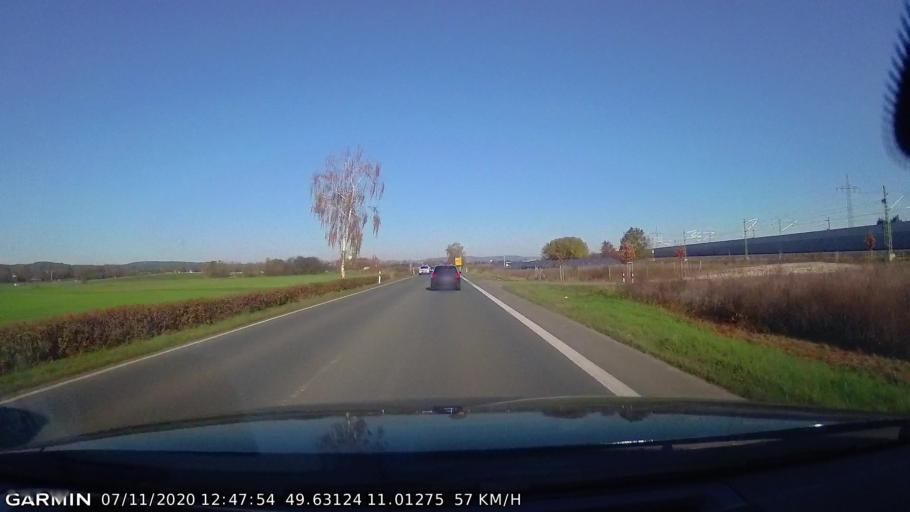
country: DE
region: Bavaria
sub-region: Regierungsbezirk Mittelfranken
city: Bubenreuth
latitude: 49.6314
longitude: 11.0128
